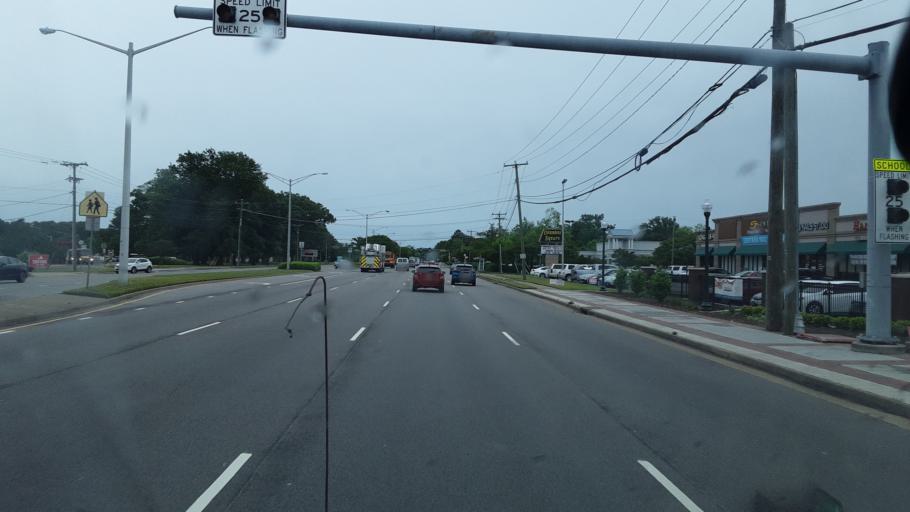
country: US
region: Virginia
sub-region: City of Chesapeake
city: Chesapeake
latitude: 36.8434
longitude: -76.1300
